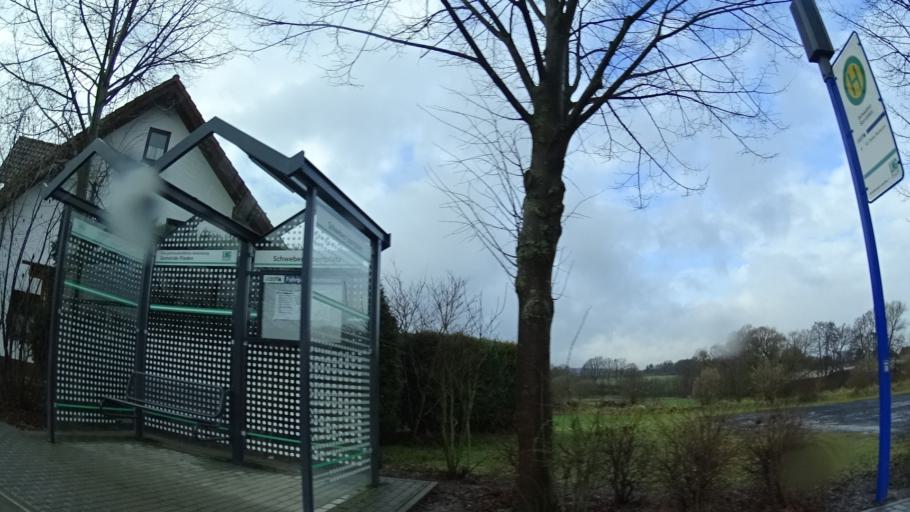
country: DE
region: Hesse
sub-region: Regierungsbezirk Kassel
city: Flieden
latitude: 50.4265
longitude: 9.5978
